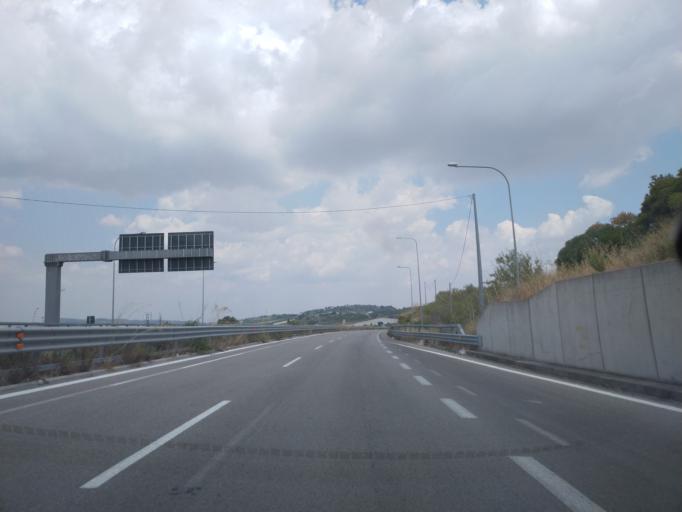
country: IT
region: Sicily
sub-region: Agrigento
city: Canicatti
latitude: 37.3833
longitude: 13.8152
